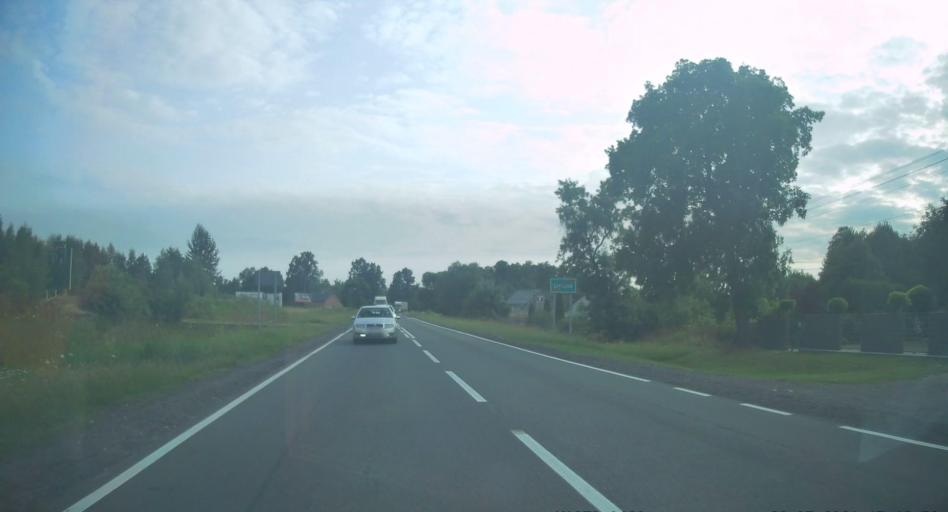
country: PL
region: Silesian Voivodeship
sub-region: Powiat czestochowski
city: Klomnice
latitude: 50.9310
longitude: 19.3804
